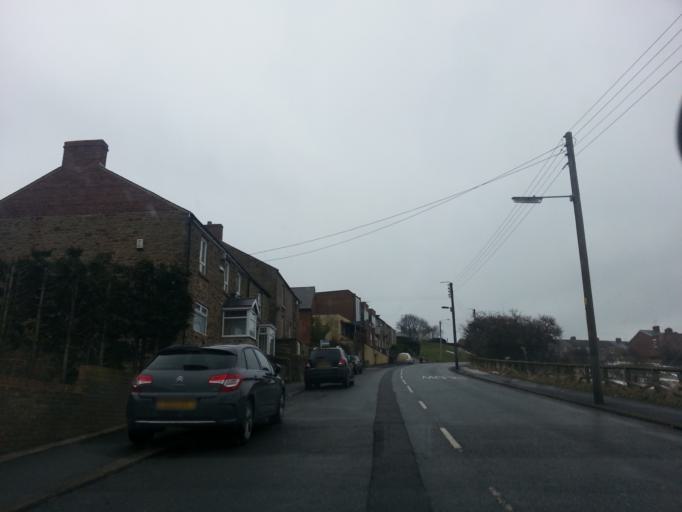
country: GB
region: England
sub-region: County Durham
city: Crook
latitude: 54.7341
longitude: -1.7482
